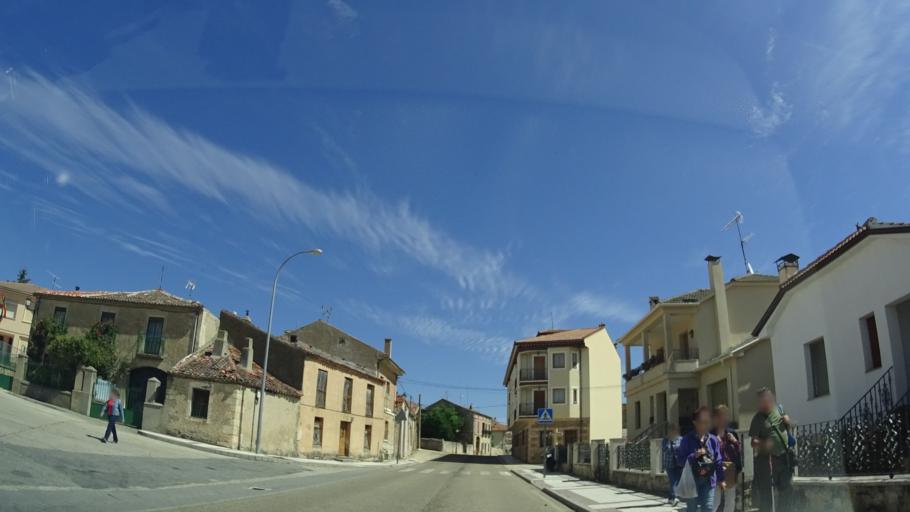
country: ES
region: Castille and Leon
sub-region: Provincia de Segovia
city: Pradena
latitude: 41.1365
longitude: -3.6882
